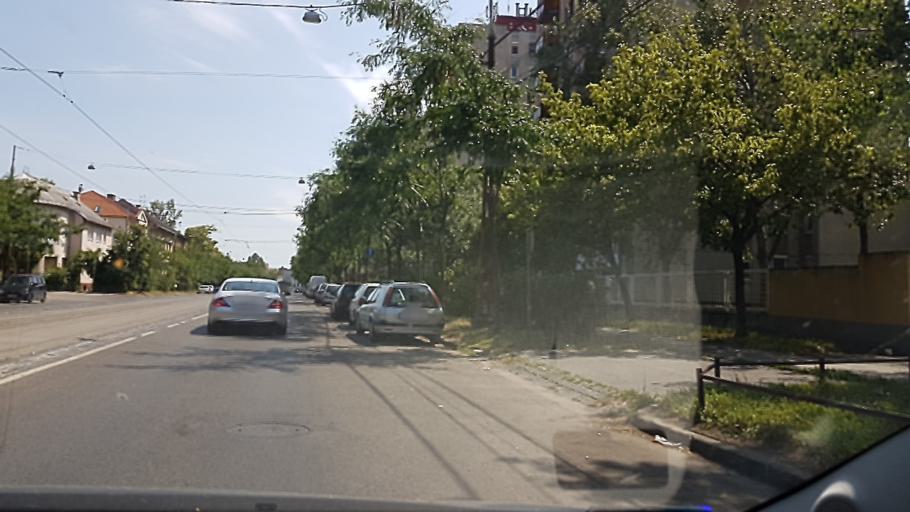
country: HU
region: Budapest
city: Budapest VIII. keruelet
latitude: 47.4850
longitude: 19.0929
